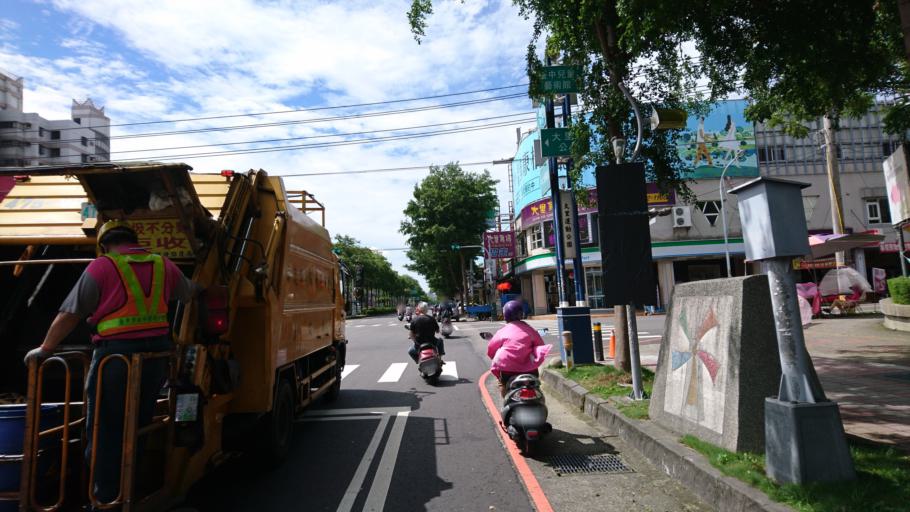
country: TW
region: Taiwan
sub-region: Taichung City
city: Taichung
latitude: 24.1003
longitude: 120.6827
